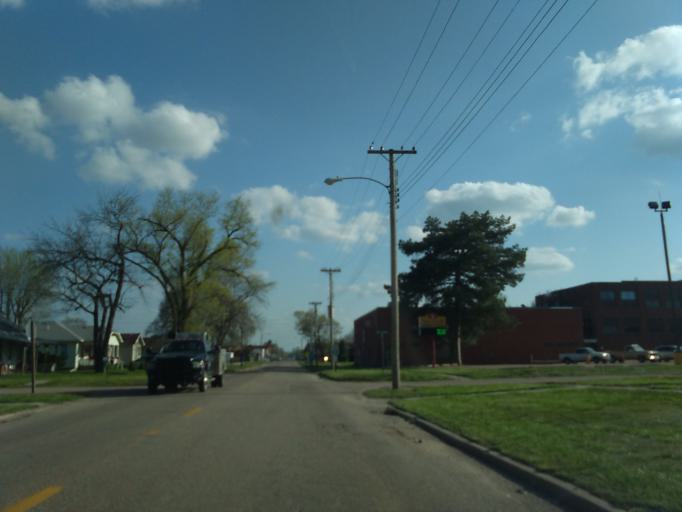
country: US
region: Nebraska
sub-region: Webster County
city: Red Cloud
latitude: 40.0933
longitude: -98.5193
